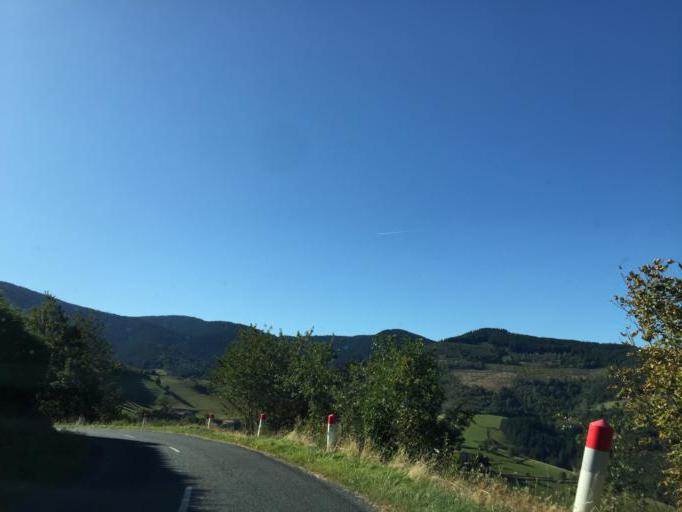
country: FR
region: Rhone-Alpes
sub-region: Departement de la Loire
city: Saint-Chamond
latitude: 45.4129
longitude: 4.5482
